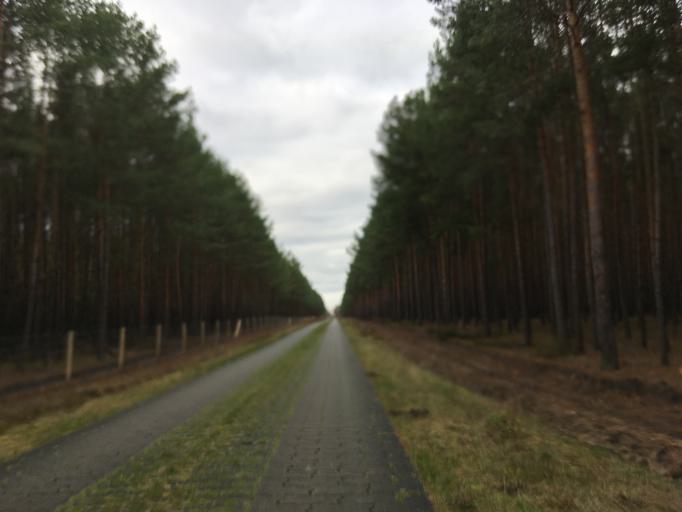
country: DE
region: Brandenburg
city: Tauer
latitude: 51.9954
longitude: 14.5136
